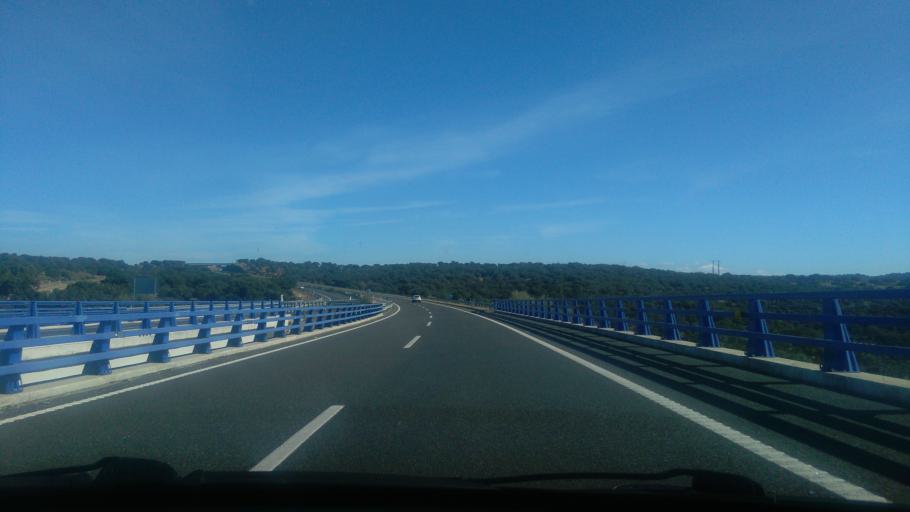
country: ES
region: Extremadura
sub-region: Provincia de Caceres
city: Plasenzuela
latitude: 39.4350
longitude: -6.0899
